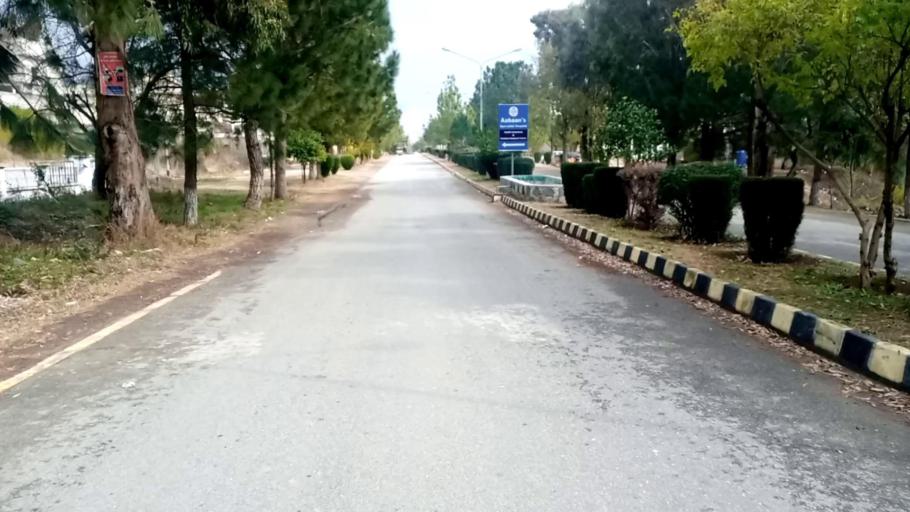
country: PK
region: Khyber Pakhtunkhwa
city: Mingora
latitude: 34.8309
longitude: 72.3498
